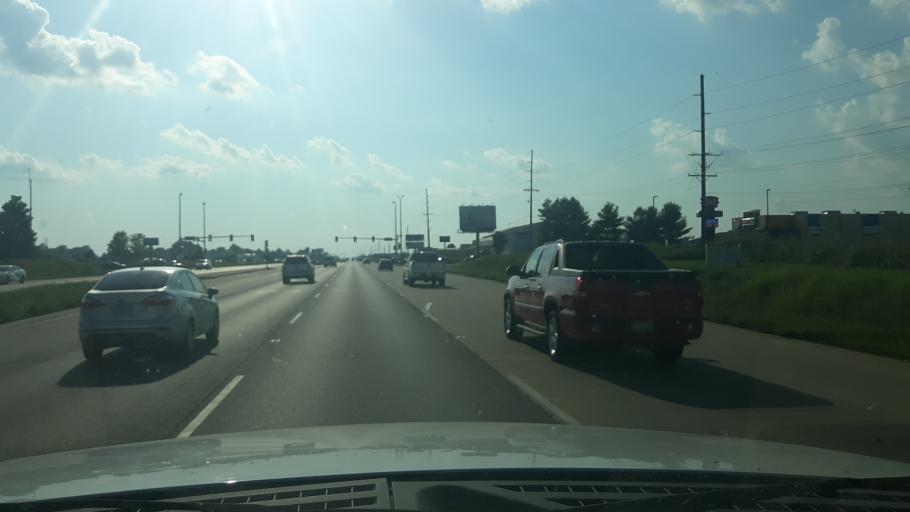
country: US
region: Illinois
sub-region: Williamson County
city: Energy
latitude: 37.7451
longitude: -88.9914
